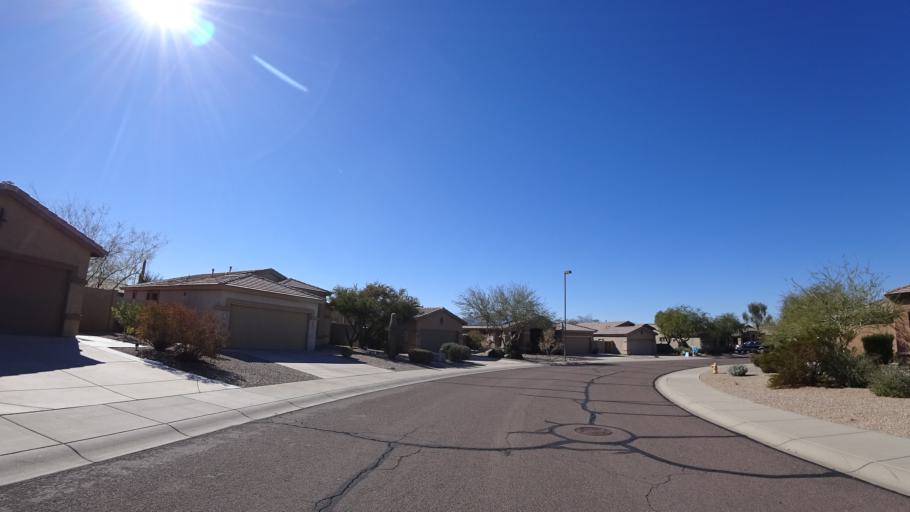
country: US
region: Arizona
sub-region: Maricopa County
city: Goodyear
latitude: 33.3519
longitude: -112.4253
